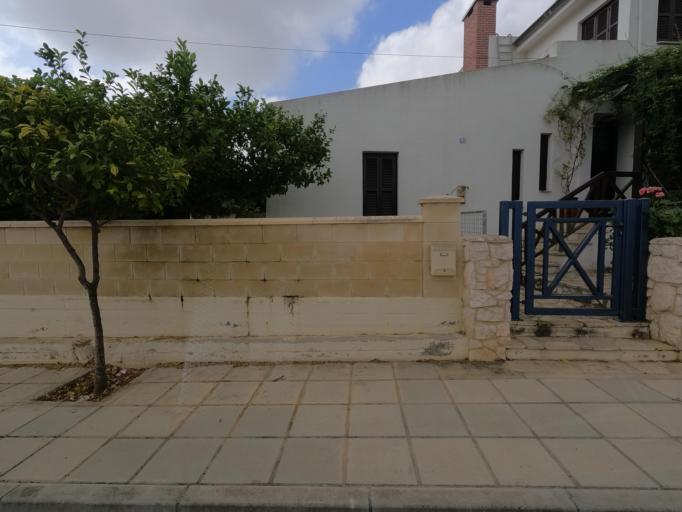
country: CY
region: Ammochostos
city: Protaras
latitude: 35.0187
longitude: 34.0279
